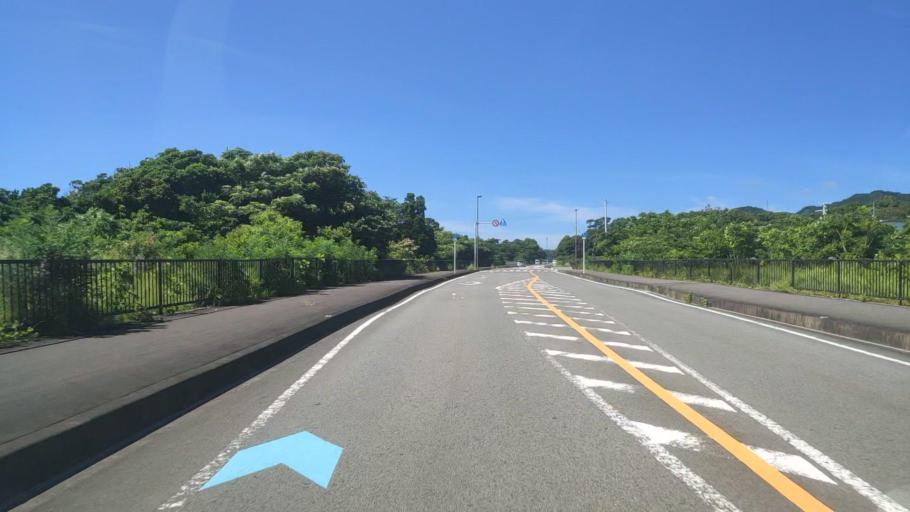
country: JP
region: Wakayama
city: Shingu
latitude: 33.7121
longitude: 135.9990
